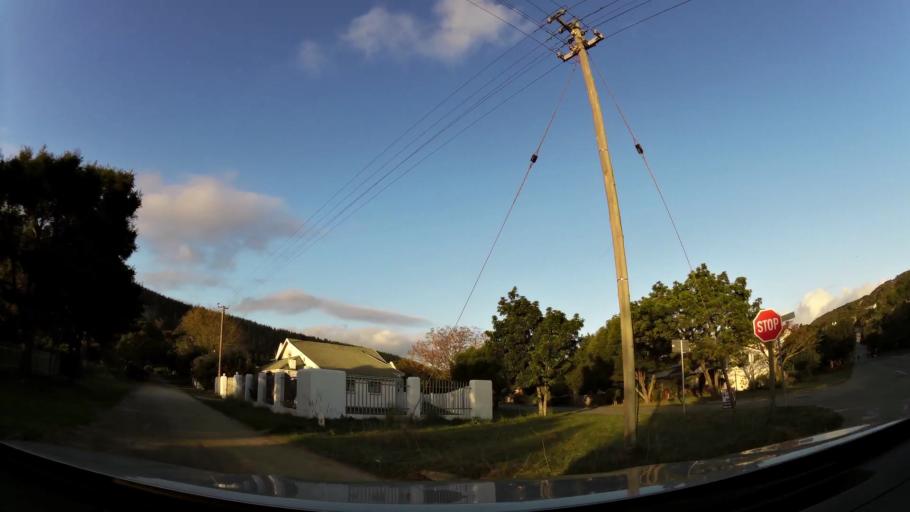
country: ZA
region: Western Cape
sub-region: Eden District Municipality
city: Knysna
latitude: -34.0193
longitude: 22.8112
